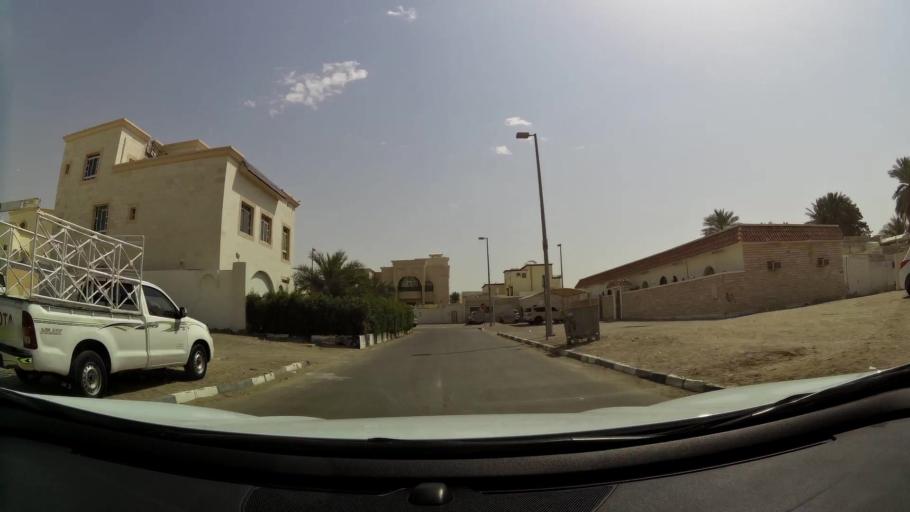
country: AE
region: Abu Dhabi
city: Abu Dhabi
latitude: 24.2971
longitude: 54.6433
